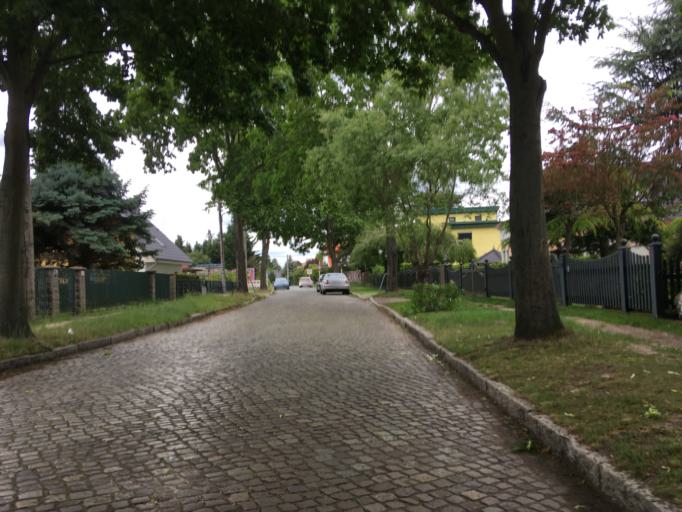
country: DE
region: Berlin
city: Biesdorf
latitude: 52.4836
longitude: 13.5741
